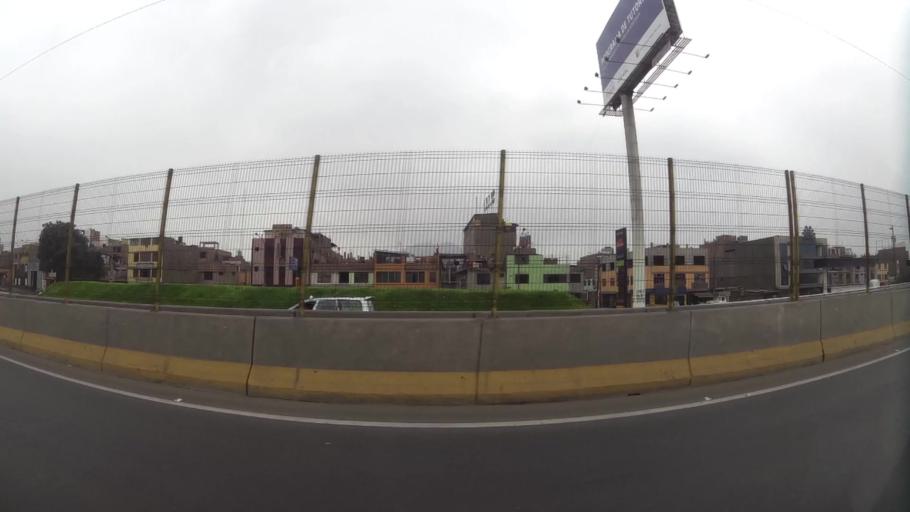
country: PE
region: Lima
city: Lima
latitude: -12.0293
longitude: -76.9988
